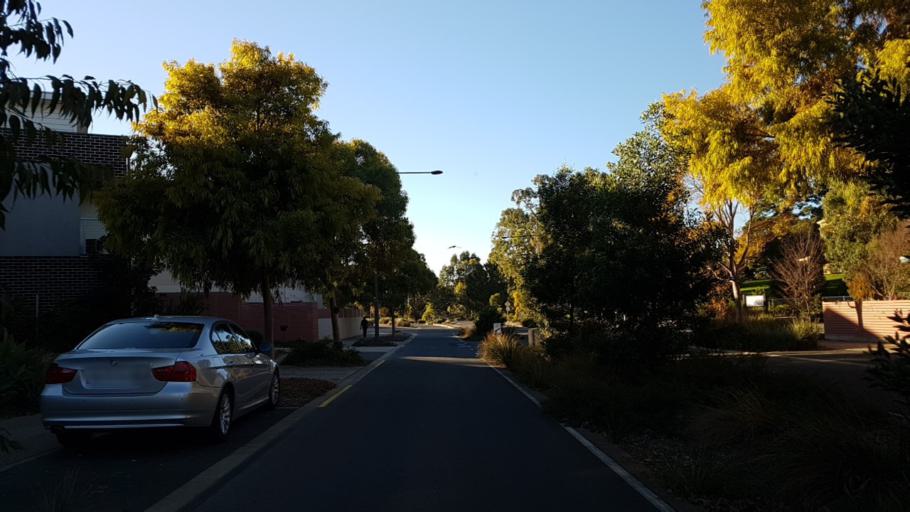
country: AU
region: South Australia
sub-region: Port Adelaide Enfield
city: Klemzig
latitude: -34.8782
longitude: 138.6503
